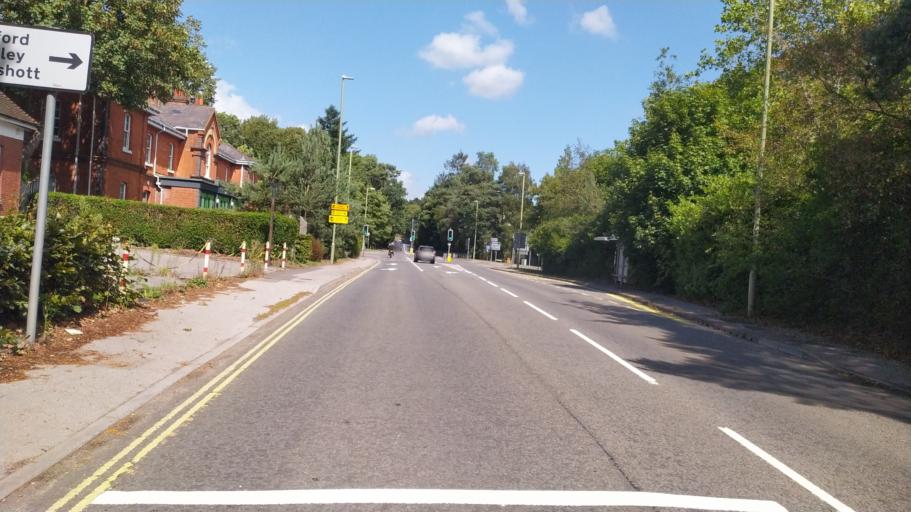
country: GB
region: England
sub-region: Hampshire
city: Bordon
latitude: 51.1215
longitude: -0.8594
